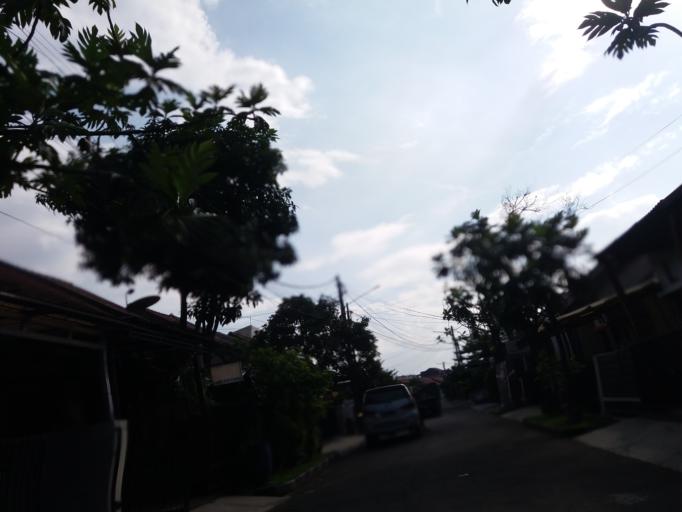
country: ID
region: West Java
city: Bandung
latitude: -6.9288
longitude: 107.6677
